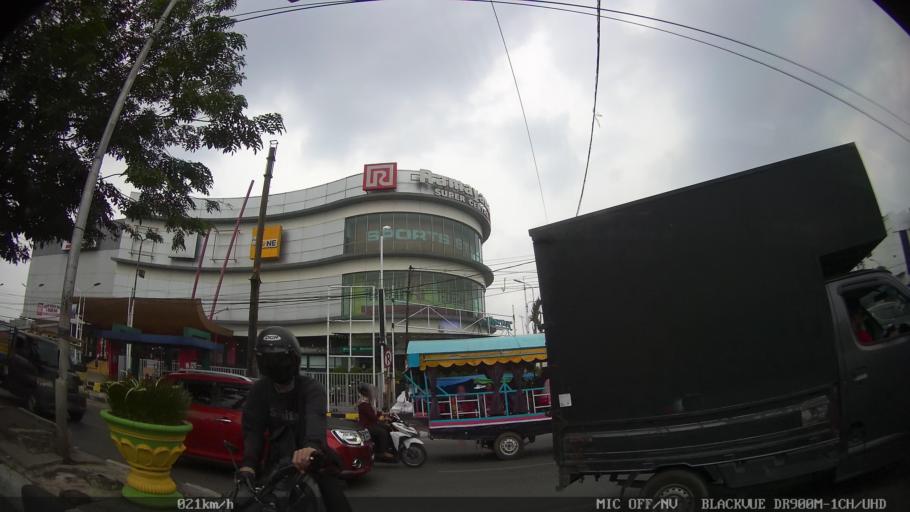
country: ID
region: North Sumatra
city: Medan
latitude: 3.5648
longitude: 98.6922
